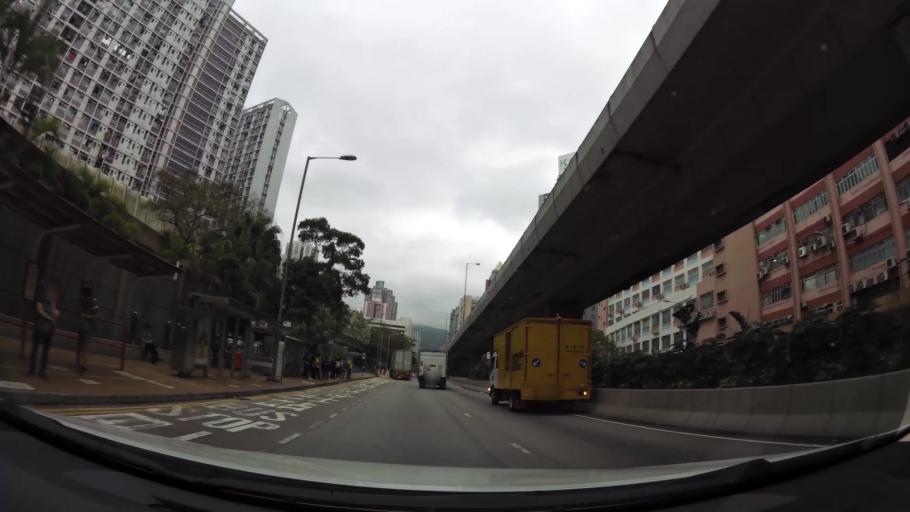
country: HK
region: Tsuen Wan
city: Tsuen Wan
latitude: 22.3596
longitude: 114.1308
